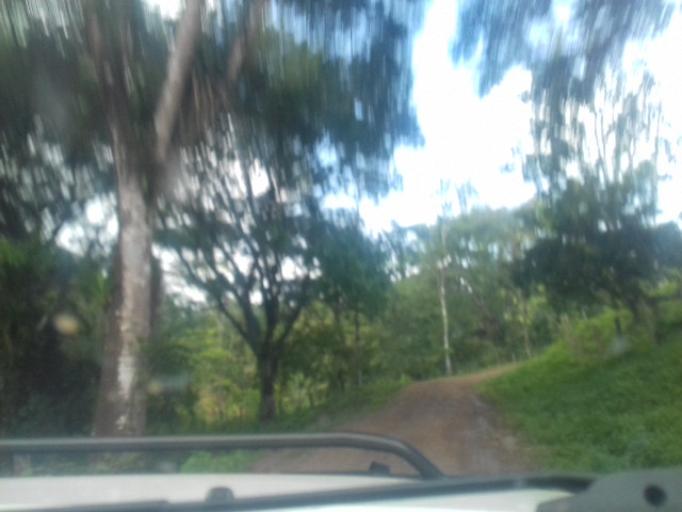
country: NI
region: Matagalpa
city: Matiguas
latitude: 12.9228
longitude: -85.3662
